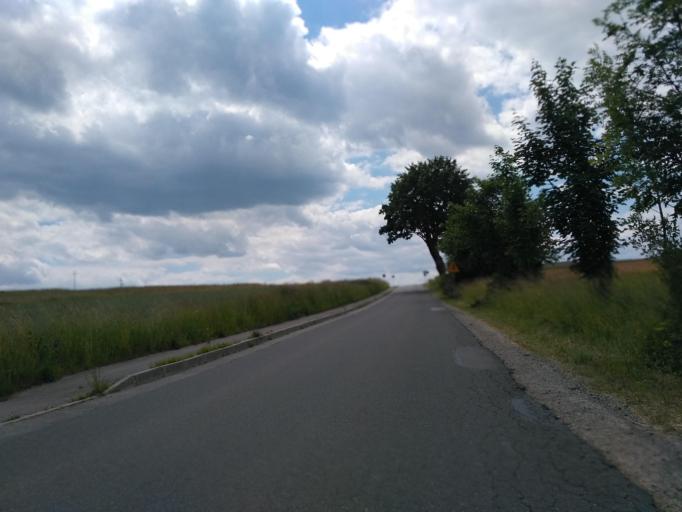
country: PL
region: Subcarpathian Voivodeship
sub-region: Powiat brzozowski
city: Nozdrzec
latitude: 49.7768
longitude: 22.2237
